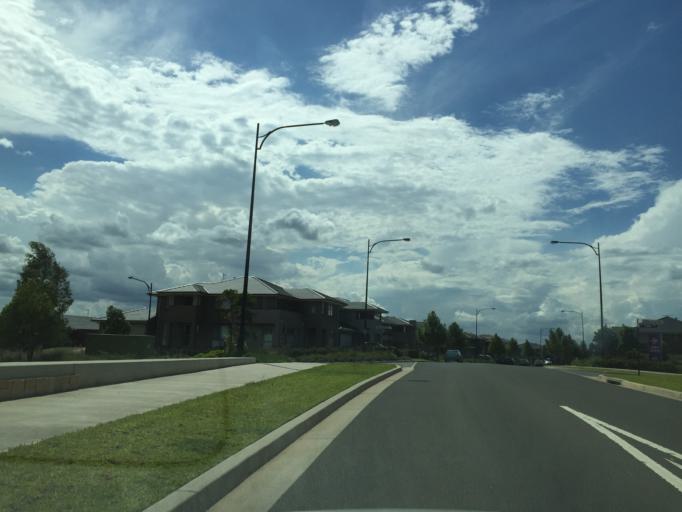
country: AU
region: New South Wales
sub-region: Blacktown
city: Doonside
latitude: -33.7789
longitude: 150.8701
